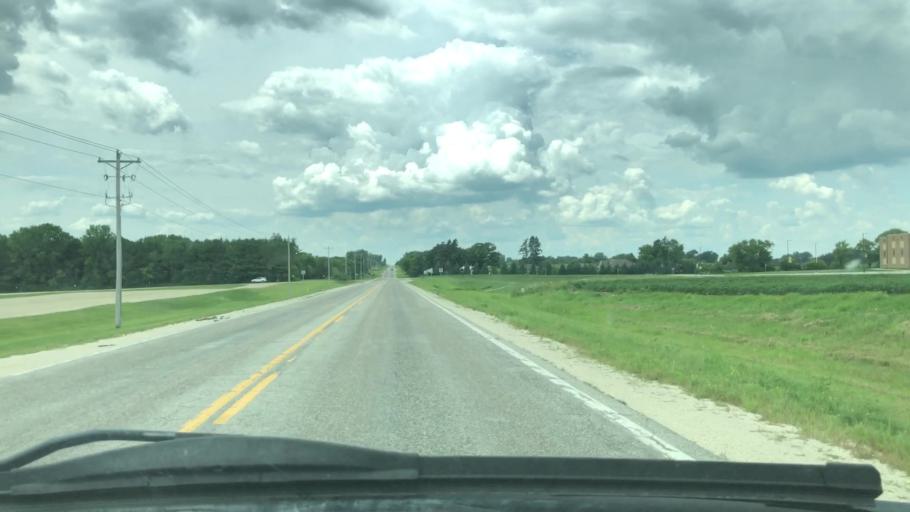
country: US
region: Minnesota
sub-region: Olmsted County
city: Stewartville
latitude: 43.8628
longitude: -92.5027
